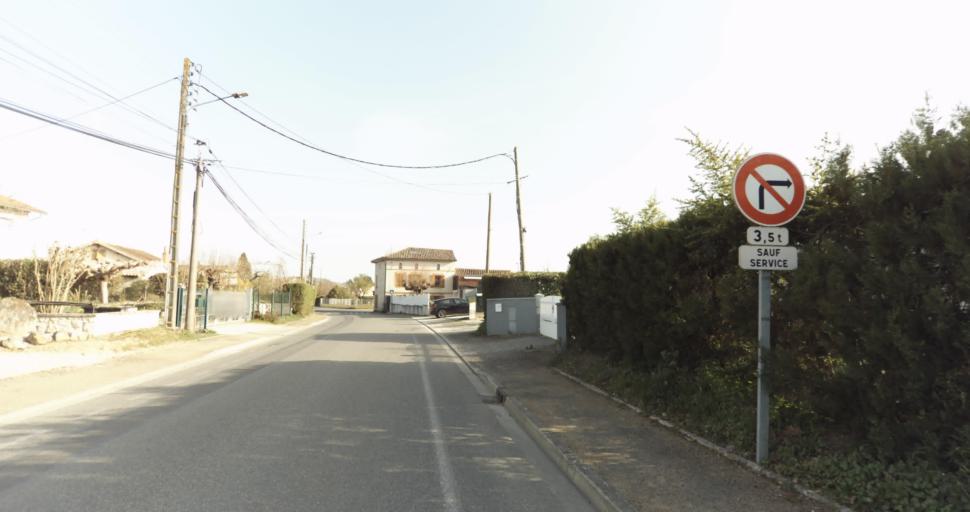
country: FR
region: Midi-Pyrenees
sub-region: Departement du Tarn
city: Saint-Sulpice-la-Pointe
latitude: 43.7673
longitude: 1.6882
